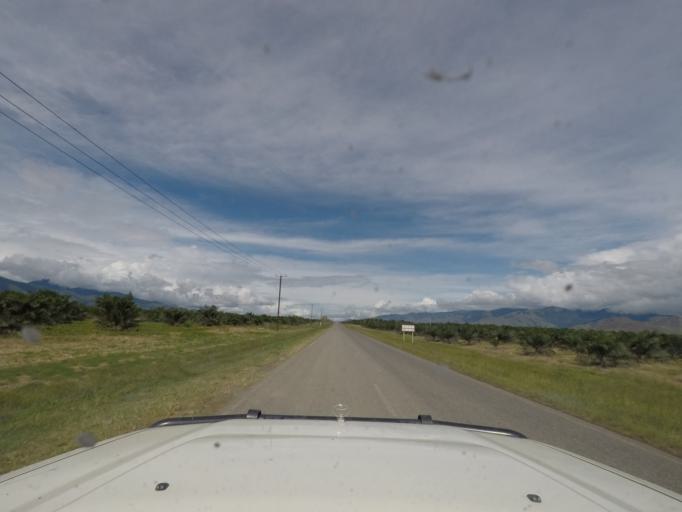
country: PG
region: Eastern Highlands
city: Kainantu
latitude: -6.0397
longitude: 145.9414
